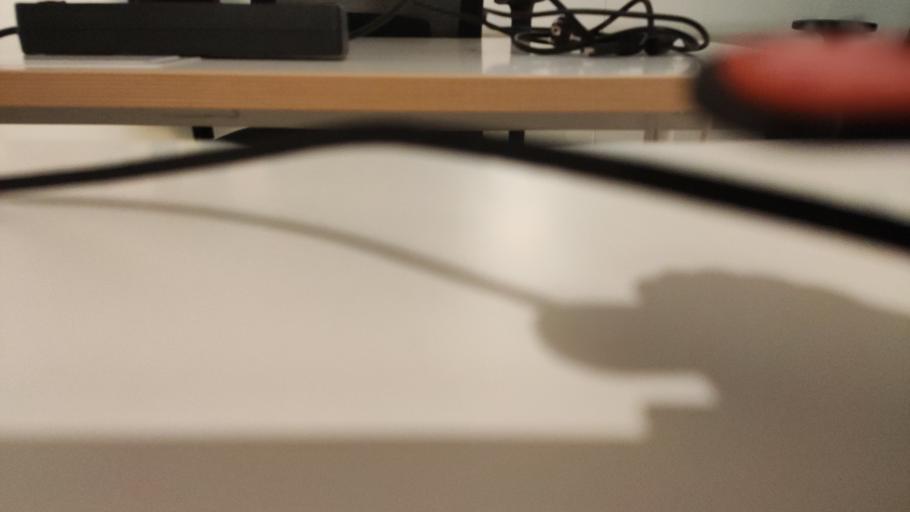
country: RU
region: Moskovskaya
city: Proletarskiy
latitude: 54.9755
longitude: 37.3844
